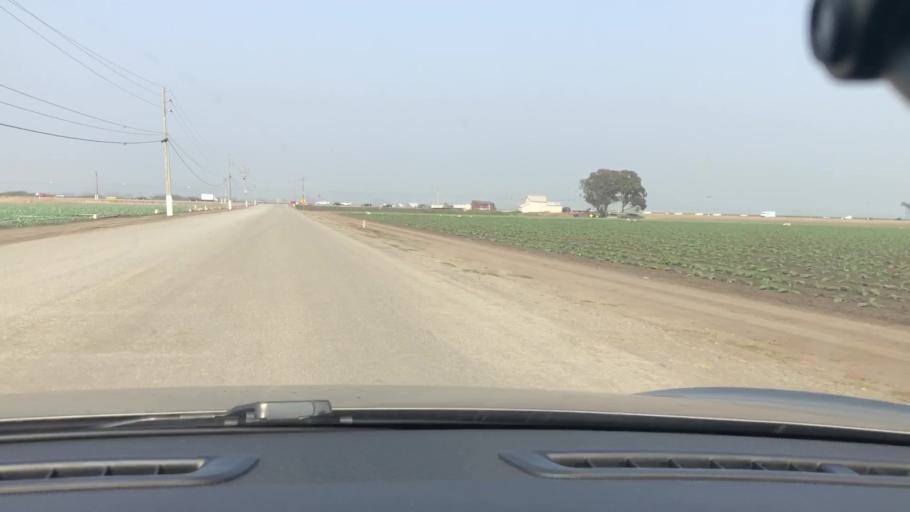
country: US
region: California
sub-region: Monterey County
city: Castroville
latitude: 36.7781
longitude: -121.7813
